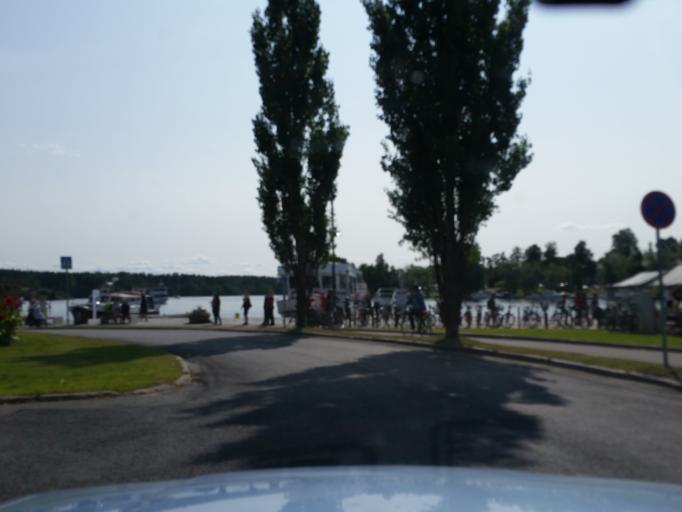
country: FI
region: Southern Savonia
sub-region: Savonlinna
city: Savonlinna
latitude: 61.8676
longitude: 28.8851
